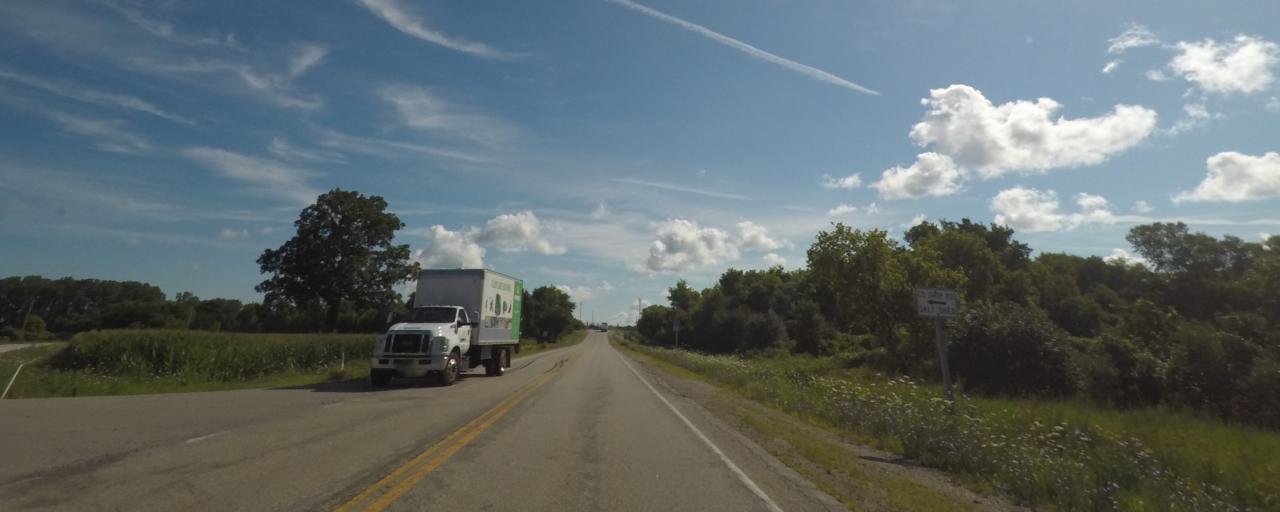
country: US
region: Wisconsin
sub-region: Jefferson County
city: Ixonia
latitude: 43.0723
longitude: -88.5970
